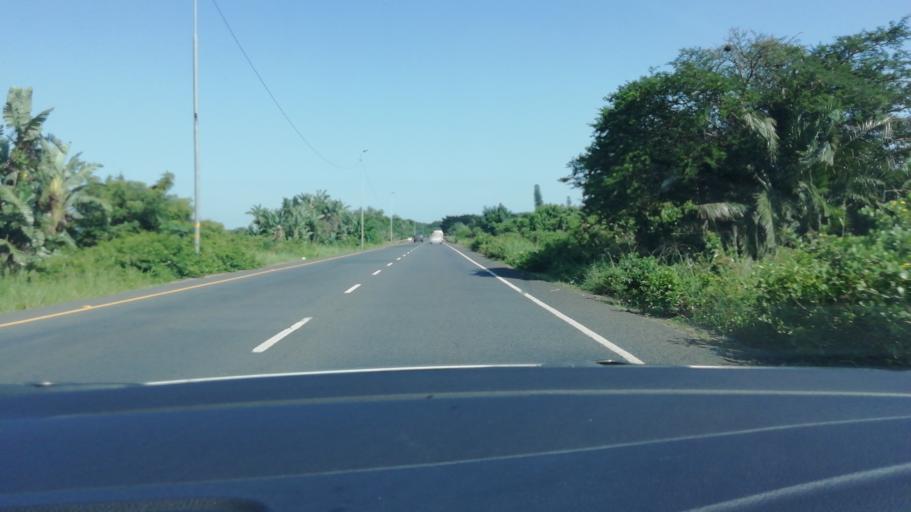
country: ZA
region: KwaZulu-Natal
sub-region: uThungulu District Municipality
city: Richards Bay
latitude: -28.7757
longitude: 32.0736
